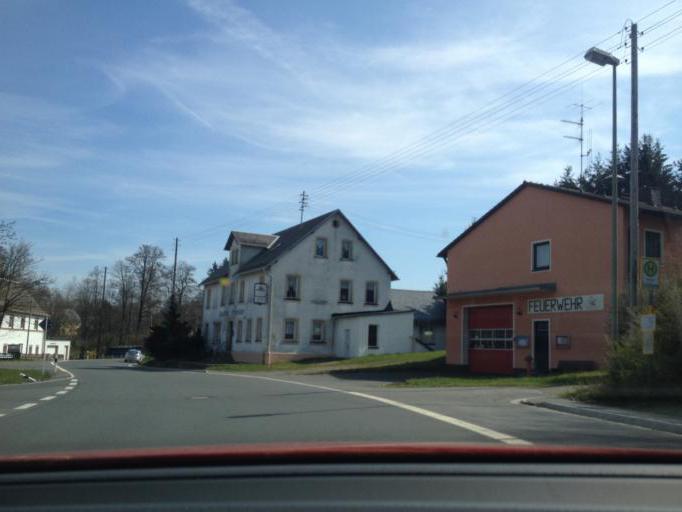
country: DE
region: Bavaria
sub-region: Upper Franconia
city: Grub
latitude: 50.0890
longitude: 11.9197
